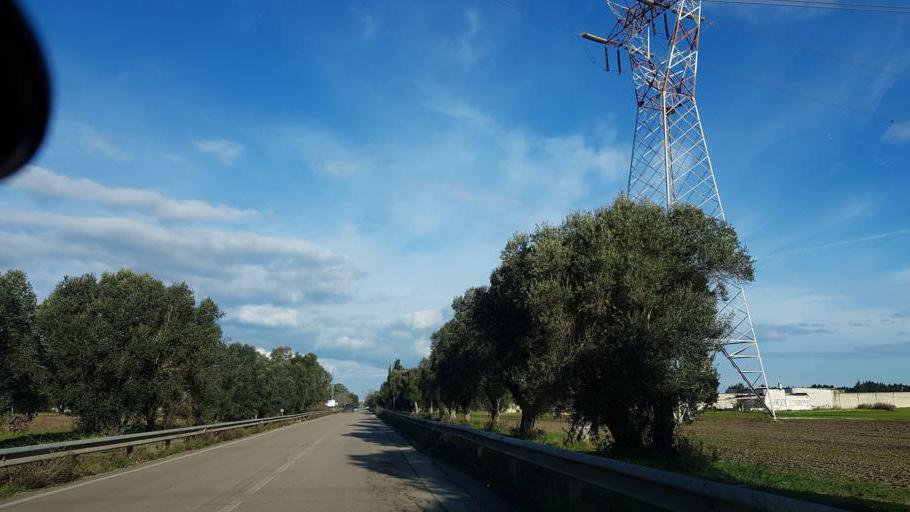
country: IT
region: Apulia
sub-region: Provincia di Brindisi
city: La Rosa
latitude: 40.6038
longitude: 17.9560
